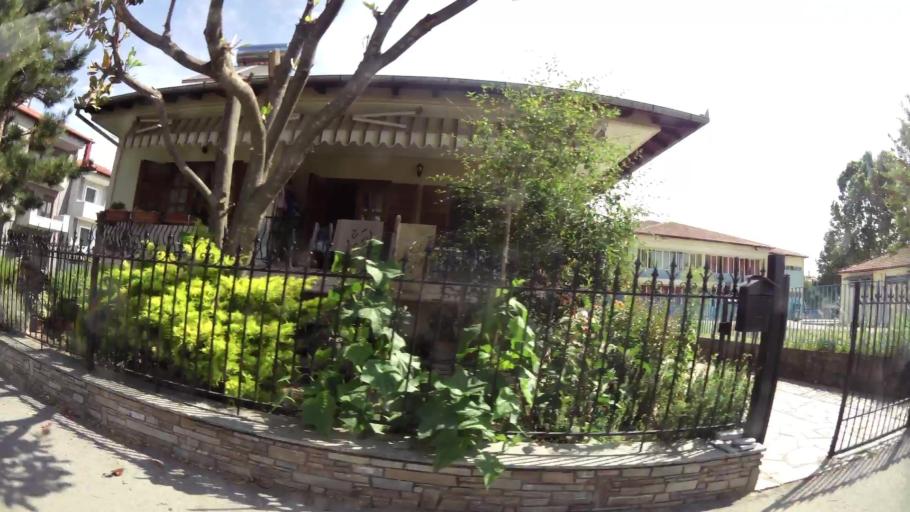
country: GR
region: Central Macedonia
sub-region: Nomos Pierias
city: Katerini
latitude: 40.2757
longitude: 22.4907
